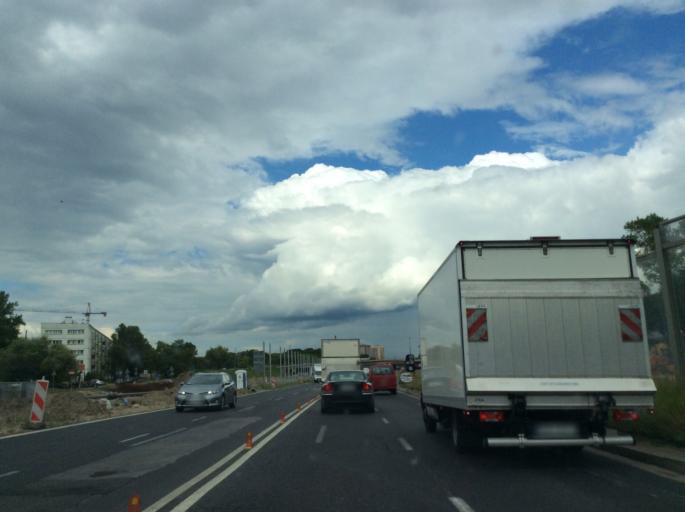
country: PL
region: Masovian Voivodeship
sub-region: Warszawa
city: Zoliborz
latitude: 52.2698
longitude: 20.9619
